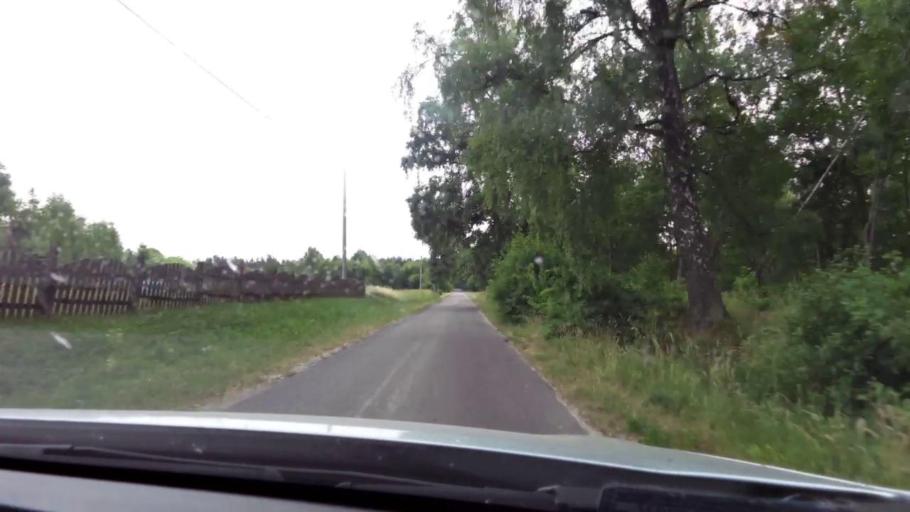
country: PL
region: Pomeranian Voivodeship
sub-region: Powiat bytowski
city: Trzebielino
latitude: 54.2467
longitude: 17.0018
